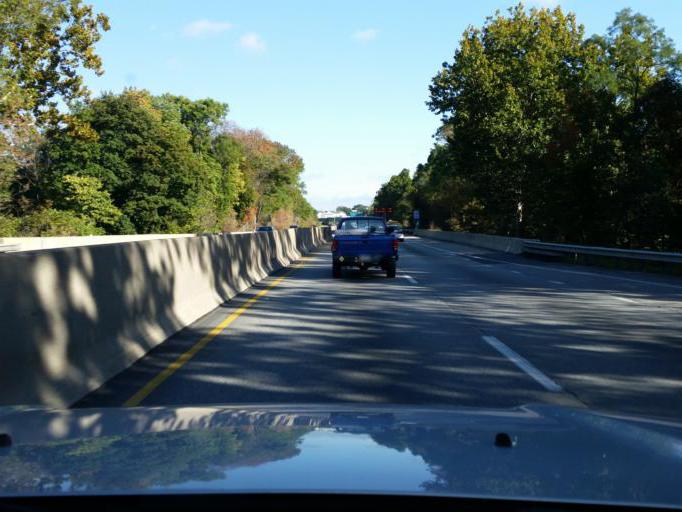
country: US
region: Pennsylvania
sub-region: Dauphin County
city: Paxtang
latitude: 40.2570
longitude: -76.8328
